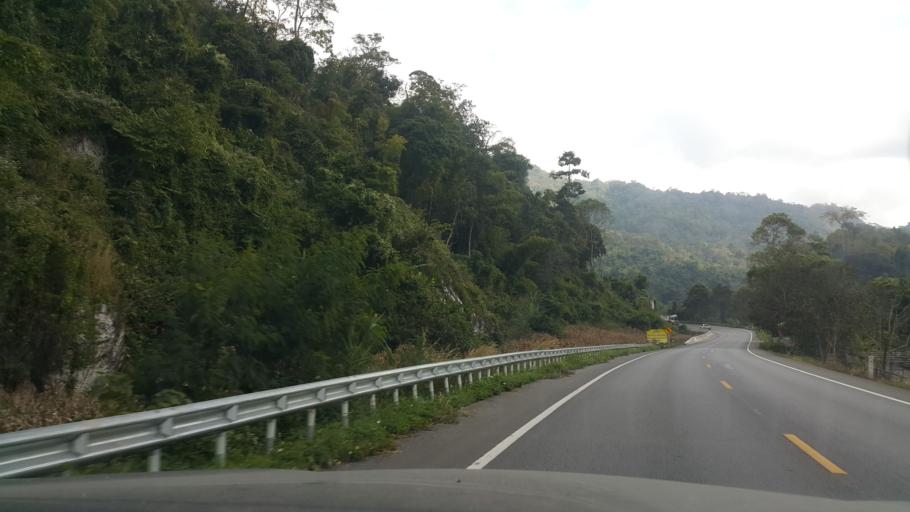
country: TH
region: Lampang
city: Wang Nuea
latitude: 19.0636
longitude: 99.7489
